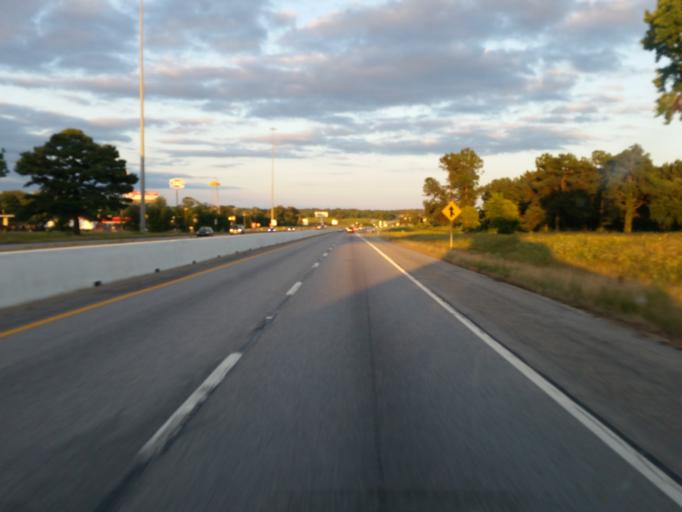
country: US
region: Texas
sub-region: Van Zandt County
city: Van
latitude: 32.5065
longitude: -95.6428
